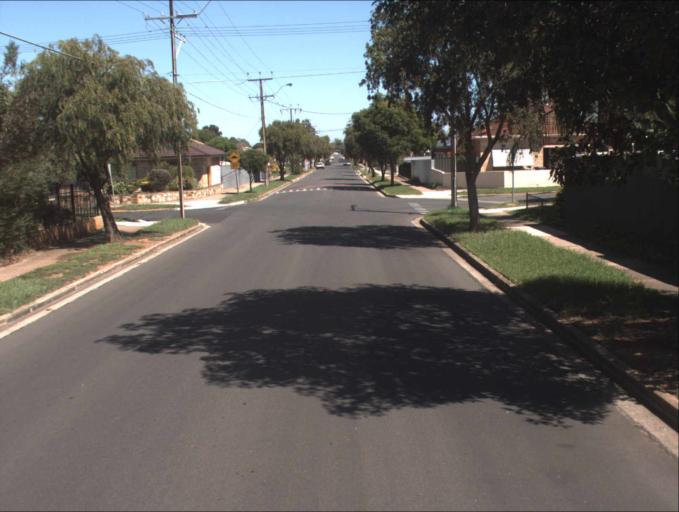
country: AU
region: South Australia
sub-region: Port Adelaide Enfield
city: Klemzig
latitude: -34.8790
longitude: 138.6454
